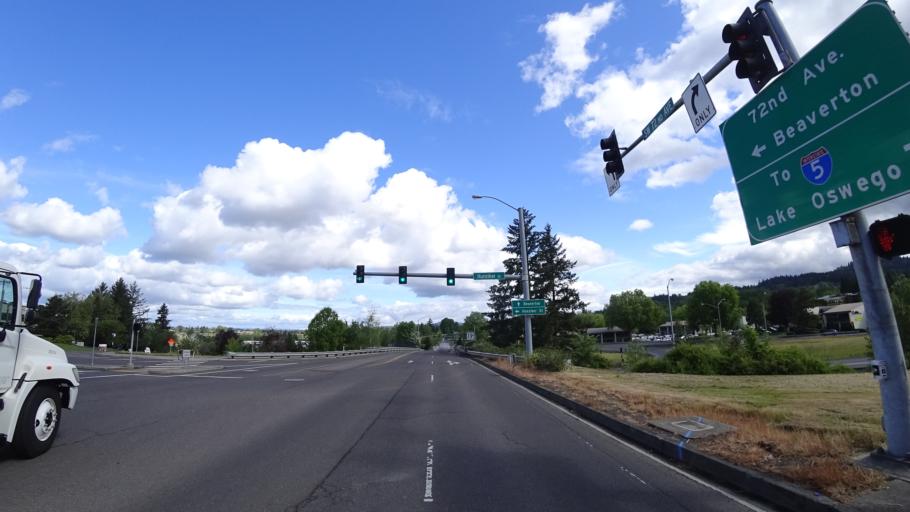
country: US
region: Oregon
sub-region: Washington County
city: Tigard
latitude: 45.4253
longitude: -122.7516
